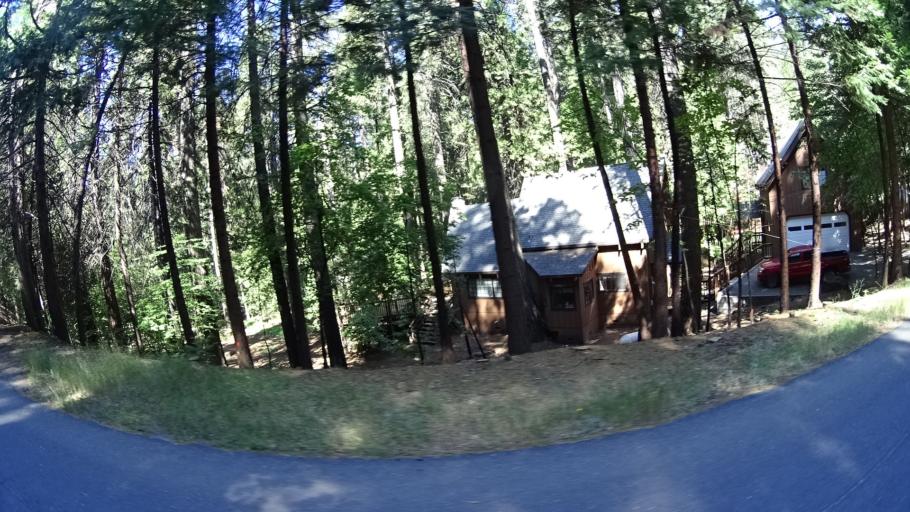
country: US
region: California
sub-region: Calaveras County
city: Arnold
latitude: 38.2437
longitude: -120.3236
